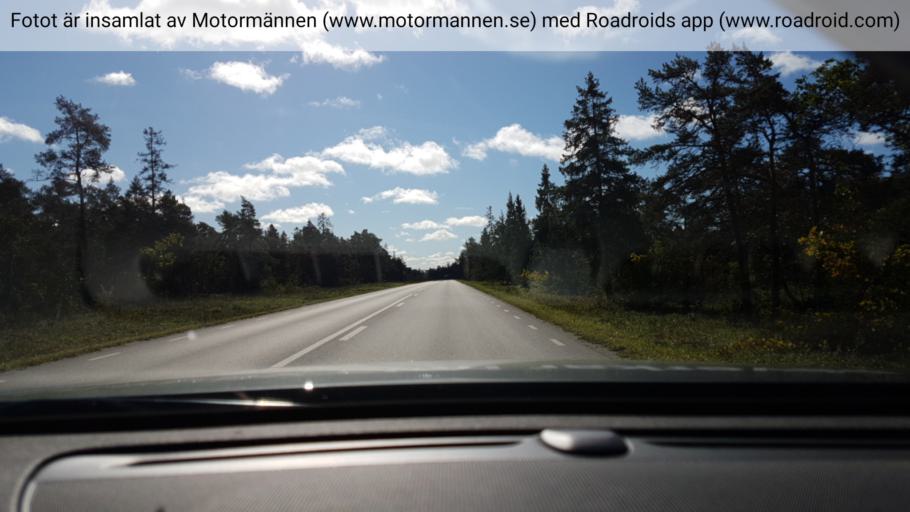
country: SE
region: Gotland
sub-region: Gotland
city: Slite
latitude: 57.7505
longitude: 18.7899
